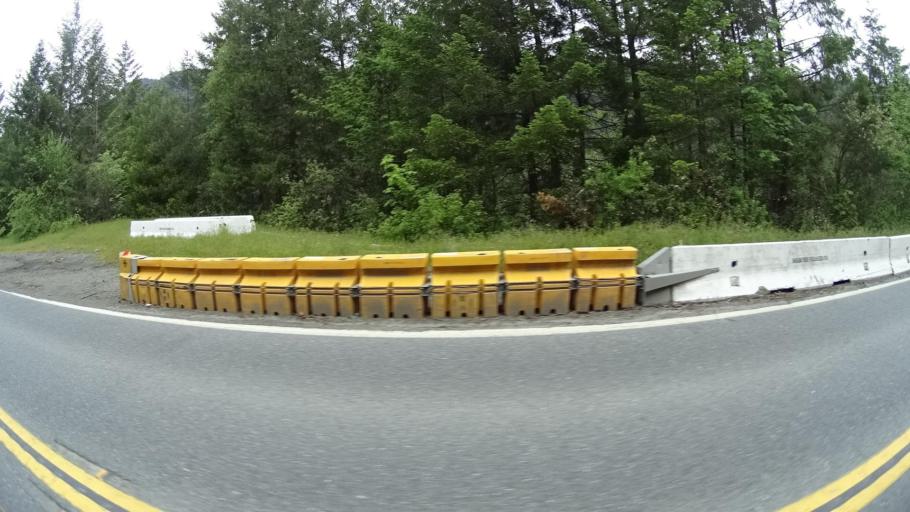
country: US
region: California
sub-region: Humboldt County
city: Willow Creek
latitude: 40.9455
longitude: -123.6539
